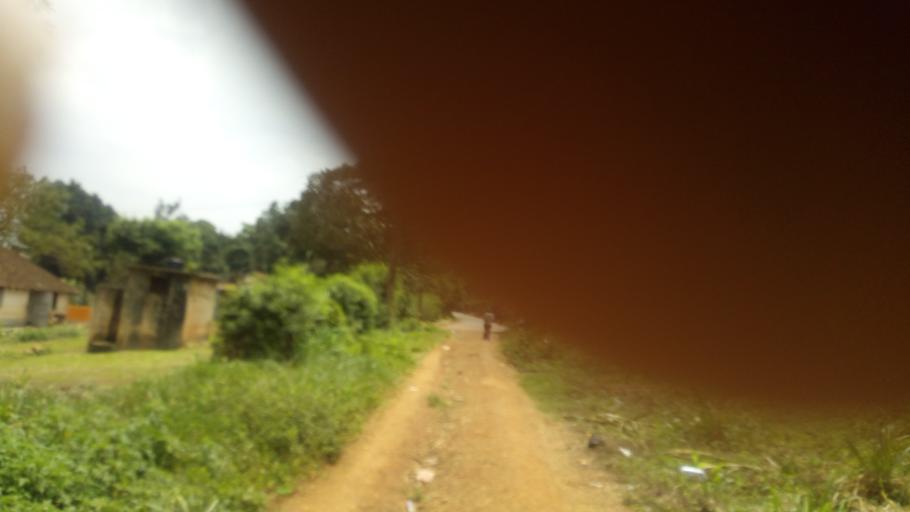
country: UG
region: Central Region
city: Kampala Central Division
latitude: 0.3318
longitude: 32.5650
